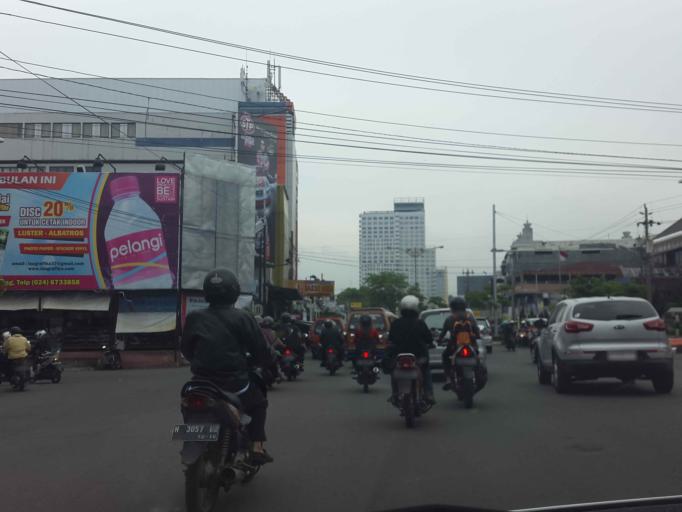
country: ID
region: Central Java
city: Semarang
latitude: -7.0007
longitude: 110.4334
